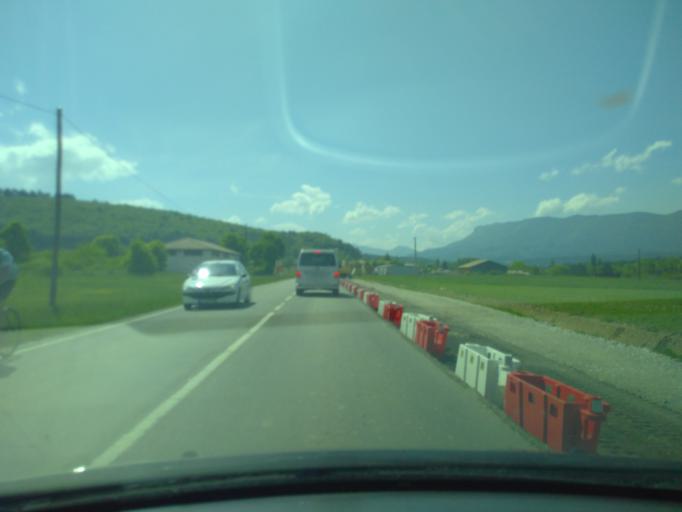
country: FR
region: Rhone-Alpes
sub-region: Departement de la Drome
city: Die
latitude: 44.7159
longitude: 5.4005
